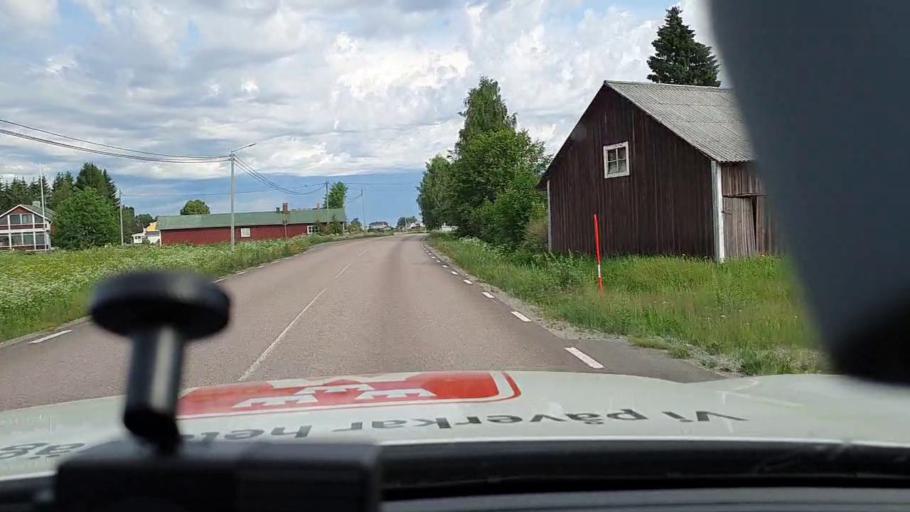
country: SE
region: Norrbotten
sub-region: Bodens Kommun
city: Saevast
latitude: 65.7026
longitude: 21.7693
